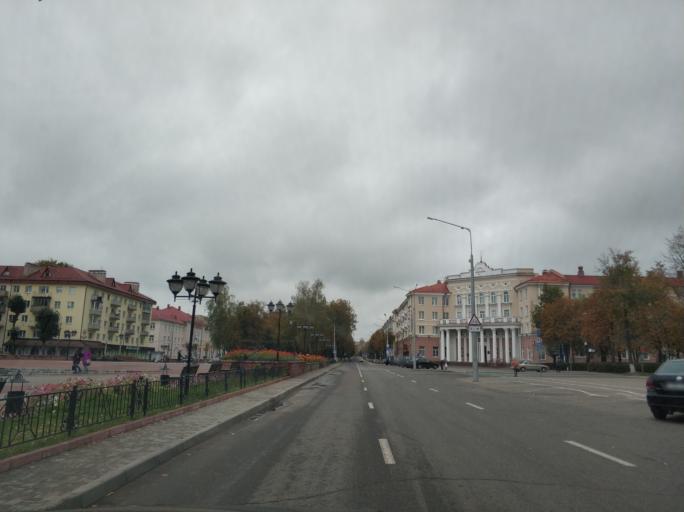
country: BY
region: Vitebsk
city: Polatsk
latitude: 55.4846
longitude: 28.7791
